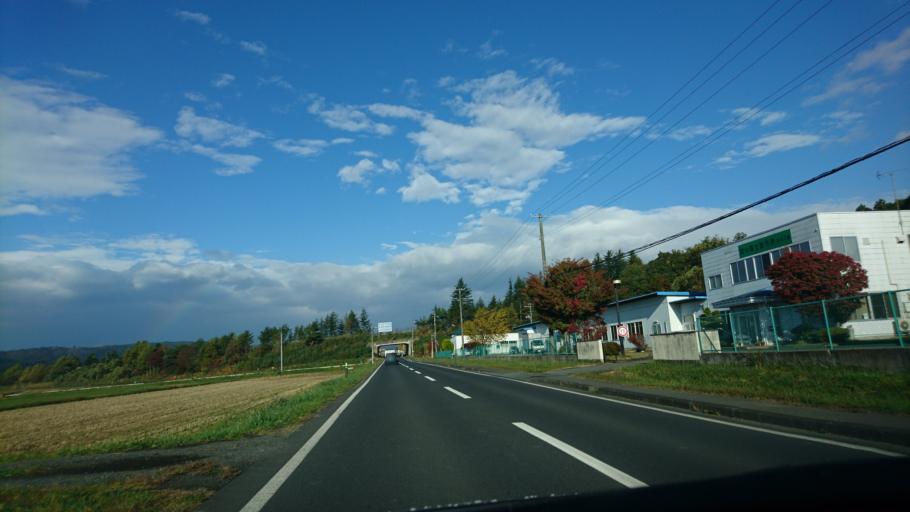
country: JP
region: Iwate
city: Ichinoseki
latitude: 39.0160
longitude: 141.1024
